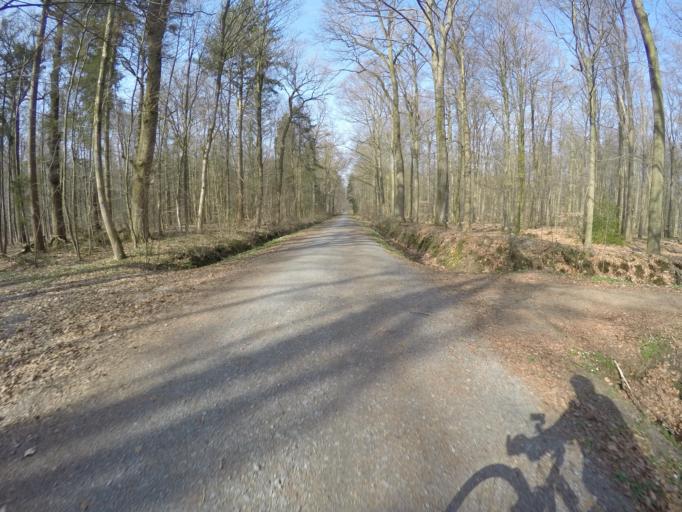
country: DE
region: Schleswig-Holstein
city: Kummerfeld
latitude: 53.7154
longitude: 9.7976
